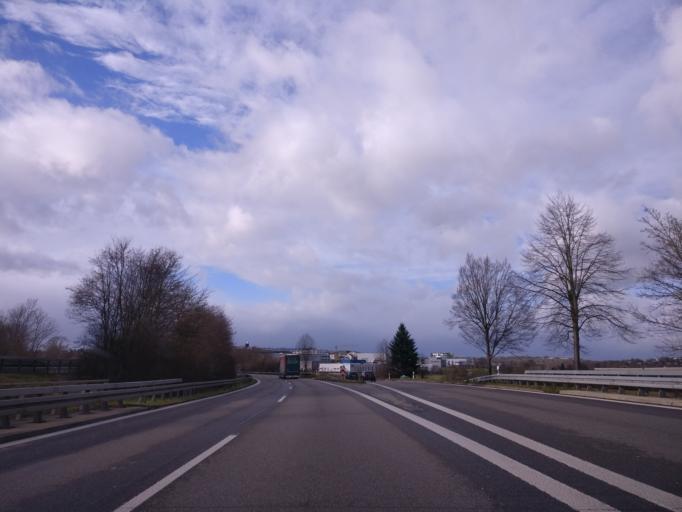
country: DE
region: Baden-Wuerttemberg
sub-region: Regierungsbezirk Stuttgart
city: Waiblingen
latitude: 48.8177
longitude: 9.3340
